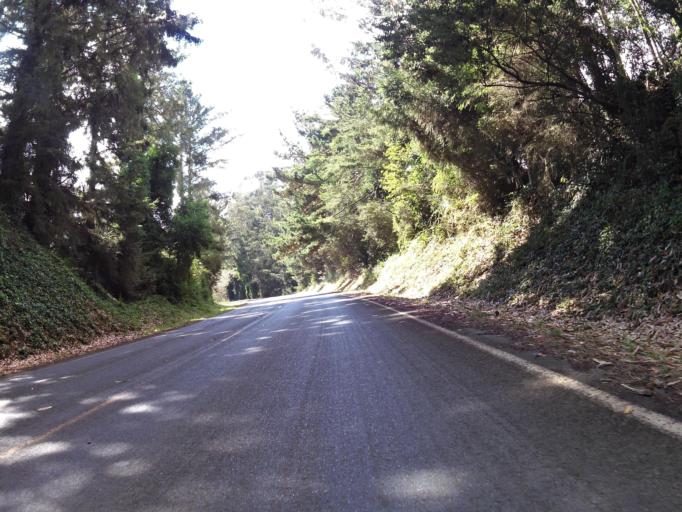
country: US
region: California
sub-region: Humboldt County
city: Humboldt Hill
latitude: 40.6546
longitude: -124.2184
